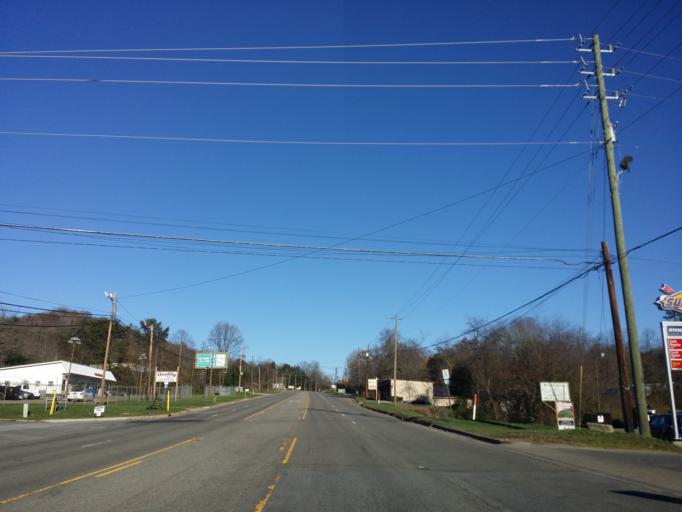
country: US
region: North Carolina
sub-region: Buncombe County
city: Swannanoa
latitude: 35.5949
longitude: -82.4256
